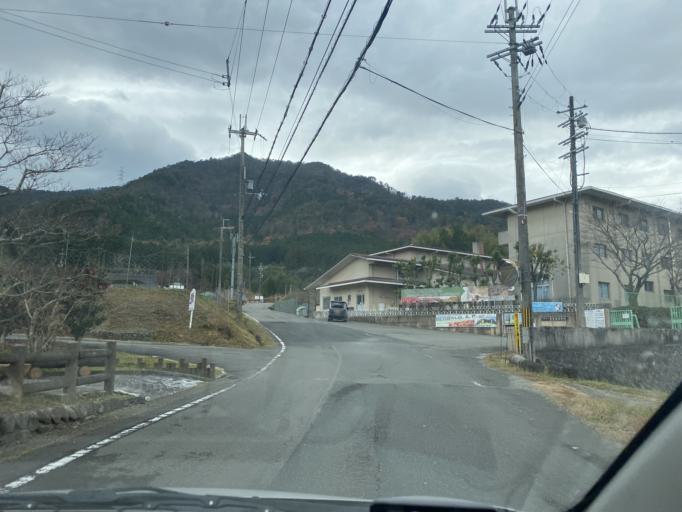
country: JP
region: Kyoto
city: Kameoka
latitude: 35.0554
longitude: 135.4566
